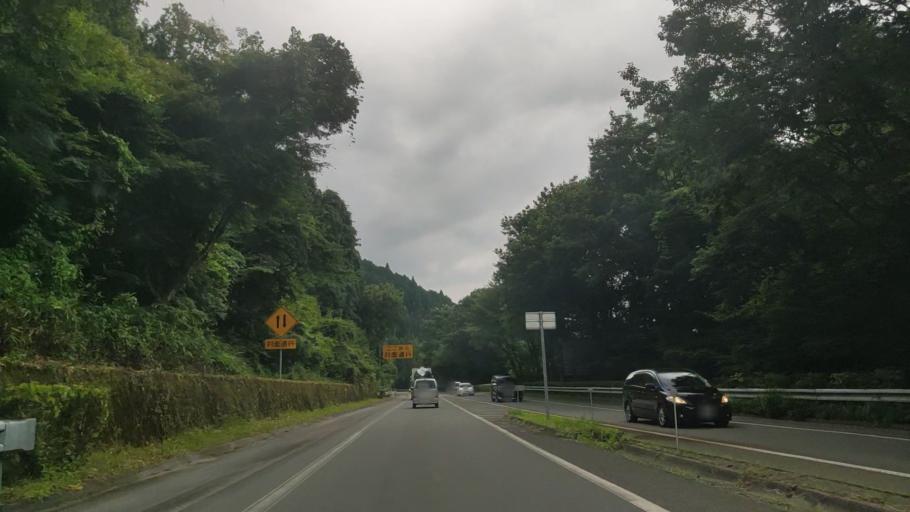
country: JP
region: Tochigi
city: Nikko
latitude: 36.7425
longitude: 139.6206
